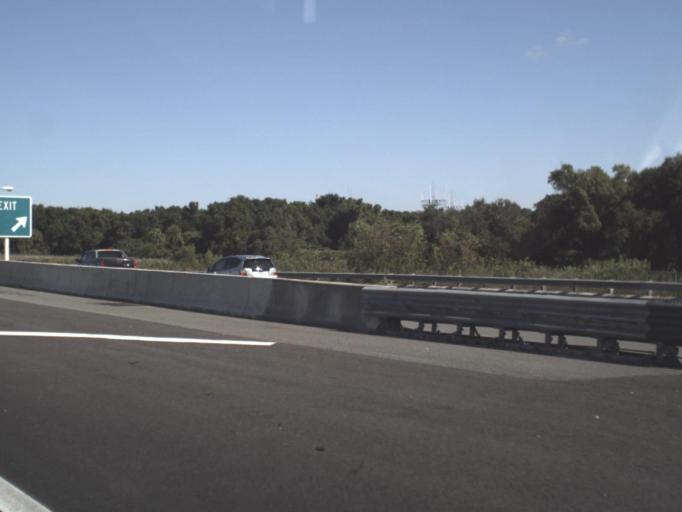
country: US
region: Florida
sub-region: Hillsborough County
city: Town 'n' Country
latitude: 27.9787
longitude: -82.5462
